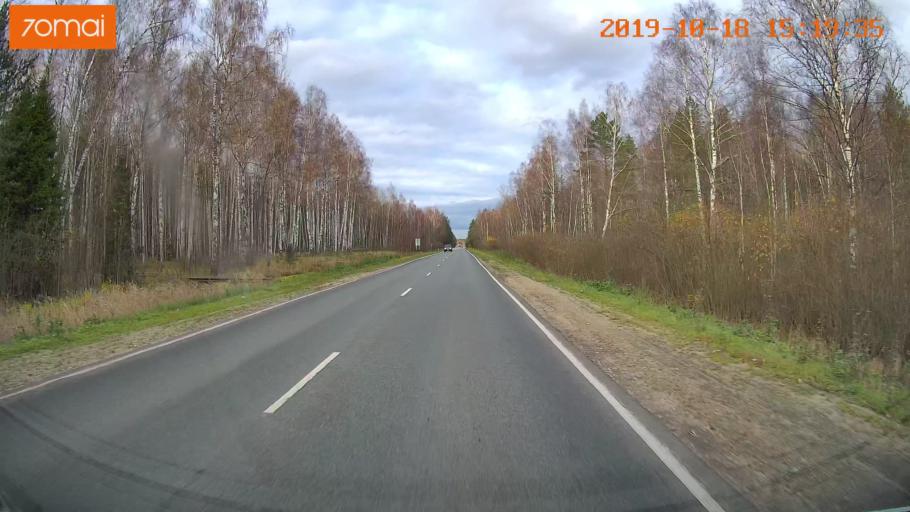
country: RU
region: Vladimir
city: Anopino
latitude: 55.6753
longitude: 40.7388
